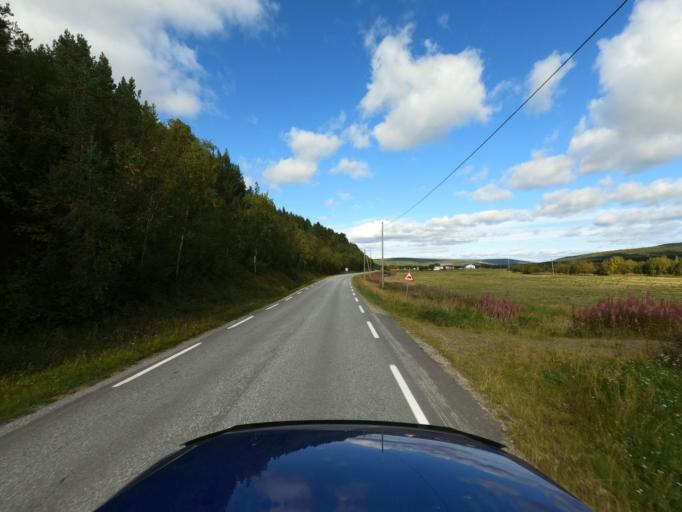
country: NO
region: Finnmark Fylke
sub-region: Karasjok
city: Karasjohka
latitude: 69.4074
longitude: 25.8075
